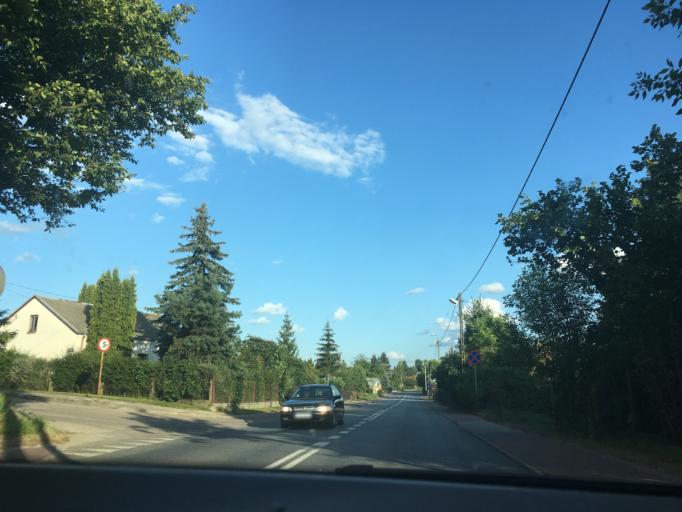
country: PL
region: Masovian Voivodeship
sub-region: Powiat losicki
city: Sarnaki
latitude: 52.3179
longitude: 22.8861
